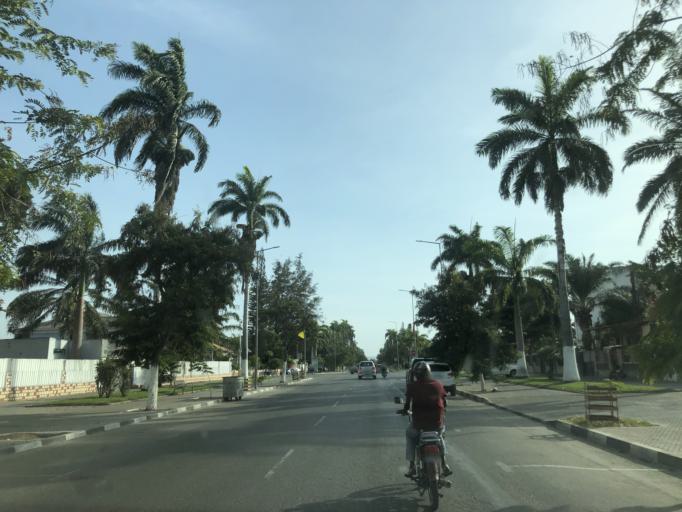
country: AO
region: Benguela
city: Benguela
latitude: -12.5773
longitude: 13.3997
